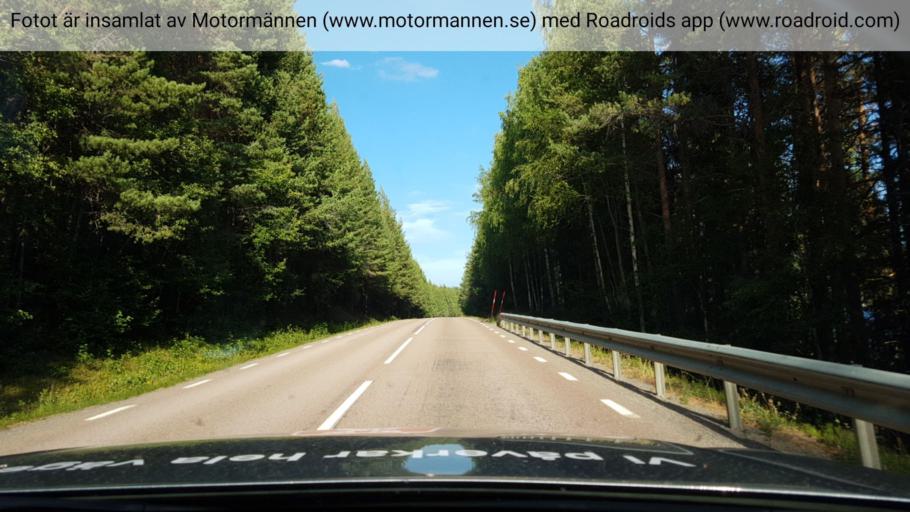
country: SE
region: Vaesternorrland
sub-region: Solleftea Kommun
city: As
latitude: 63.5876
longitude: 16.3091
